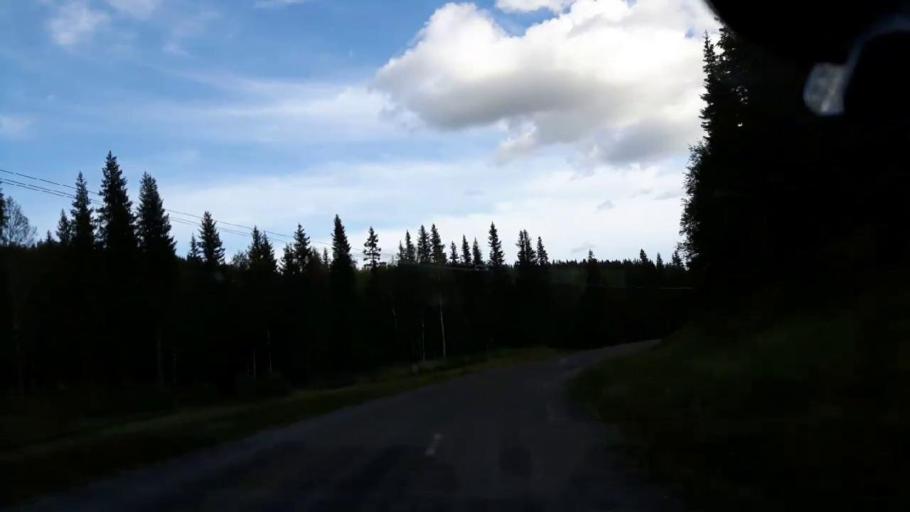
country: SE
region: Jaemtland
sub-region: Ragunda Kommun
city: Hammarstrand
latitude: 63.4212
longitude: 16.0702
